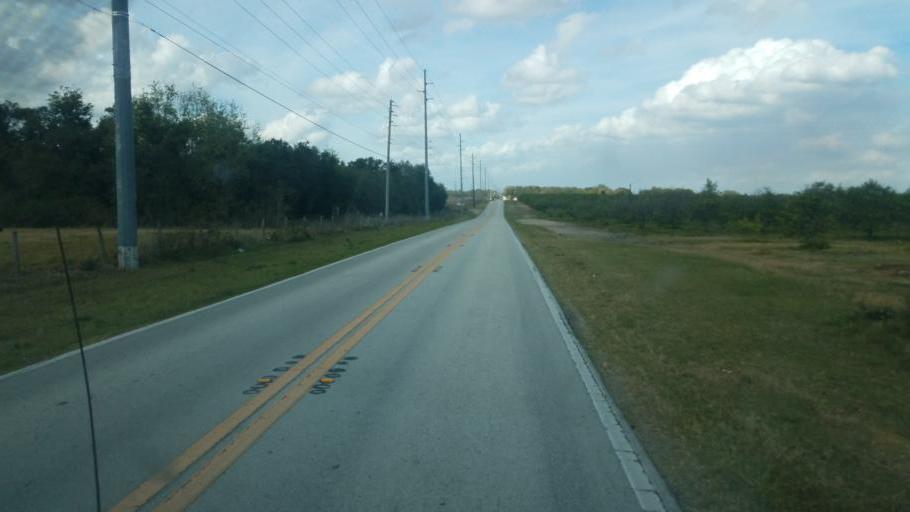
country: US
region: Florida
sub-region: Polk County
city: Haines City
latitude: 28.1226
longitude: -81.5903
